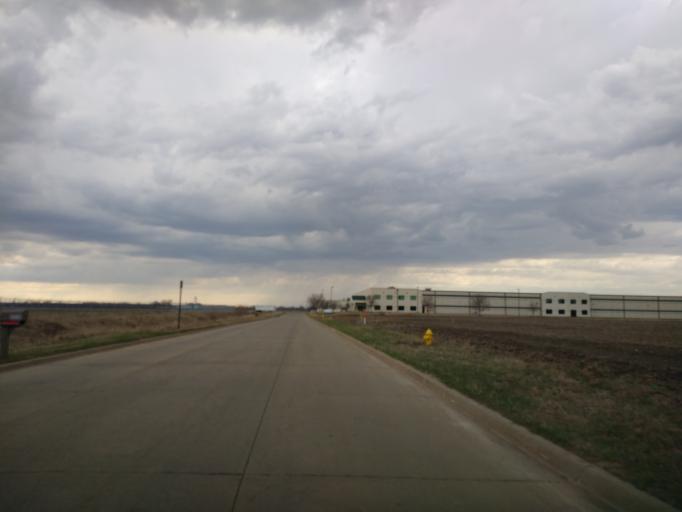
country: US
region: Iowa
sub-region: Woodbury County
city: Sergeant Bluff
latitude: 42.4148
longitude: -96.3735
